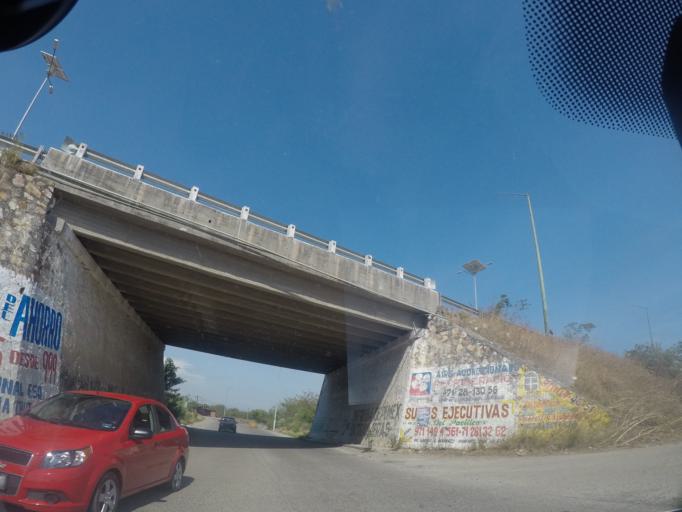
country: MX
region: Oaxaca
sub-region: Santo Domingo Tehuantepec
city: La Noria
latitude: 16.2222
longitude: -95.2089
